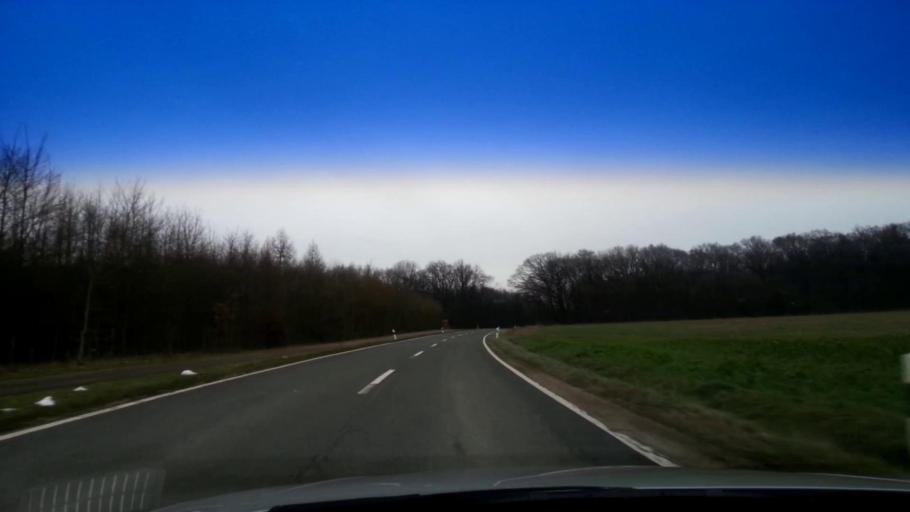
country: DE
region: Bavaria
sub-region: Upper Franconia
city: Litzendorf
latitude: 49.8896
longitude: 11.0100
